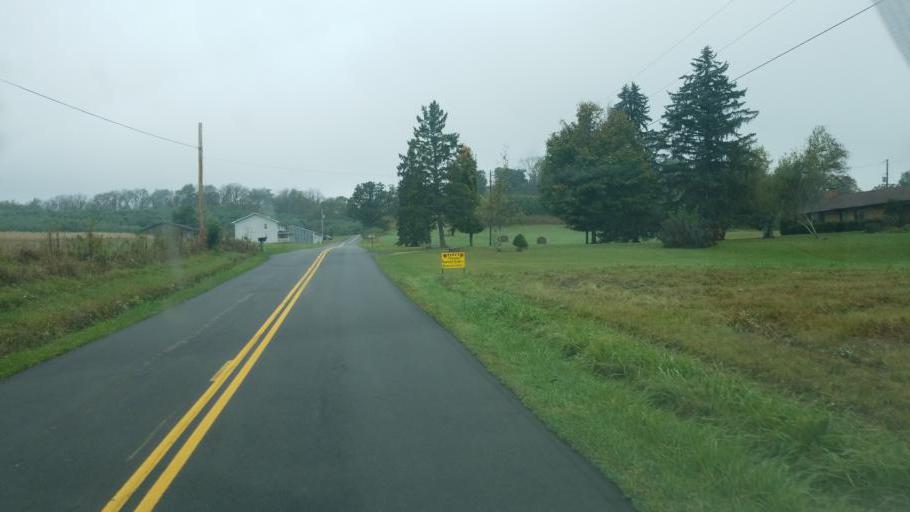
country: US
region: Ohio
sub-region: Carroll County
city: Carrollton
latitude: 40.5300
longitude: -81.1864
